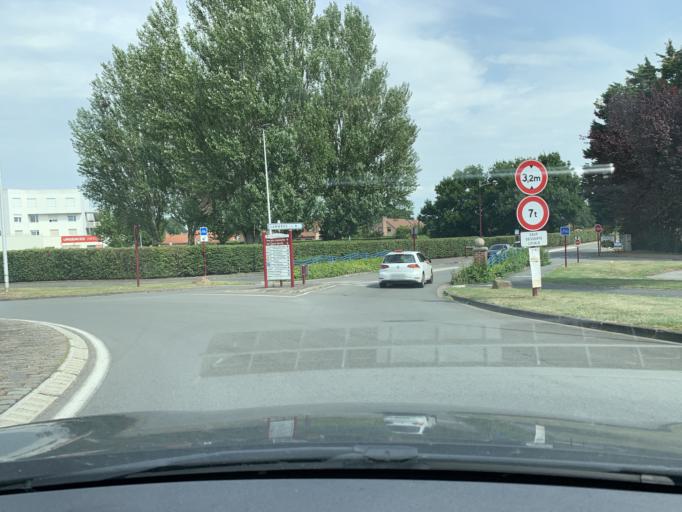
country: FR
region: Nord-Pas-de-Calais
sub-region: Departement du Nord
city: Lambres-lez-Douai
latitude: 50.3583
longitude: 3.0564
